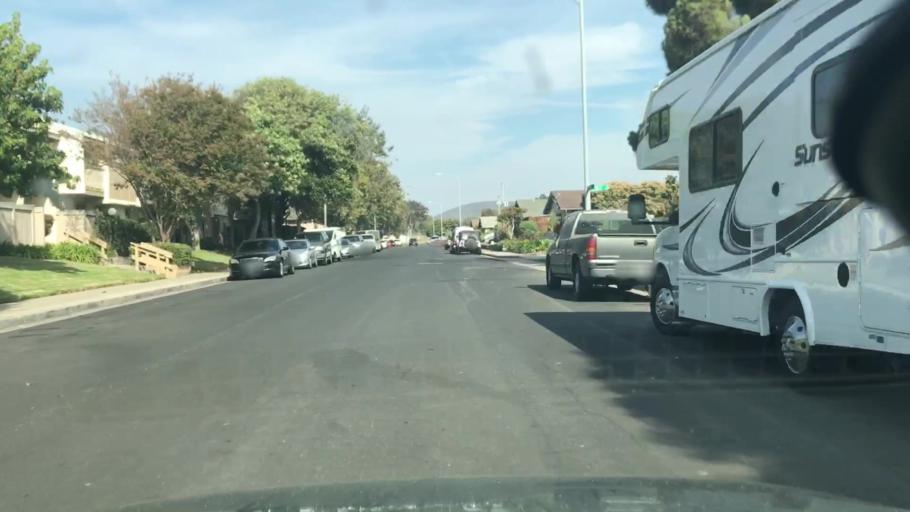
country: US
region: California
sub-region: Santa Barbara County
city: Lompoc
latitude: 34.6371
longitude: -120.4740
